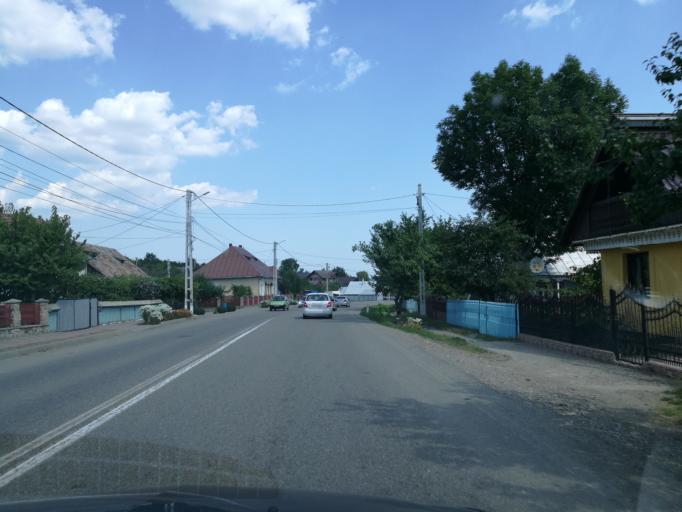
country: RO
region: Neamt
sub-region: Comuna Baltatesti
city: Baltatesti
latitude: 47.1247
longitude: 26.3105
